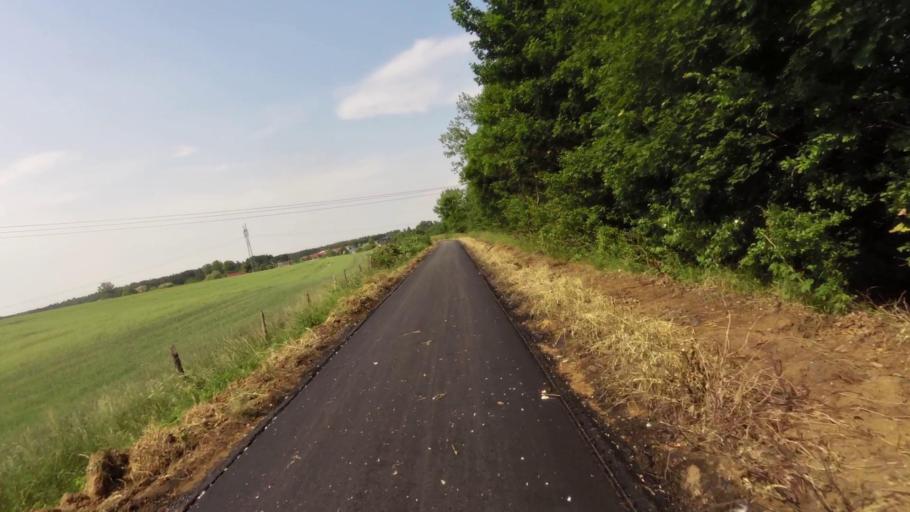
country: PL
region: West Pomeranian Voivodeship
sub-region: Powiat pyrzycki
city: Bielice
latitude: 53.2123
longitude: 14.6120
